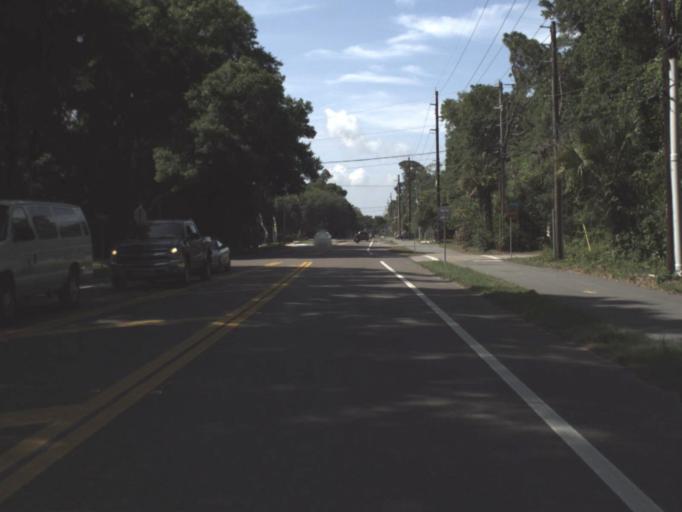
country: US
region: Florida
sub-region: Nassau County
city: Fernandina Beach
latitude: 30.5827
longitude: -81.4547
